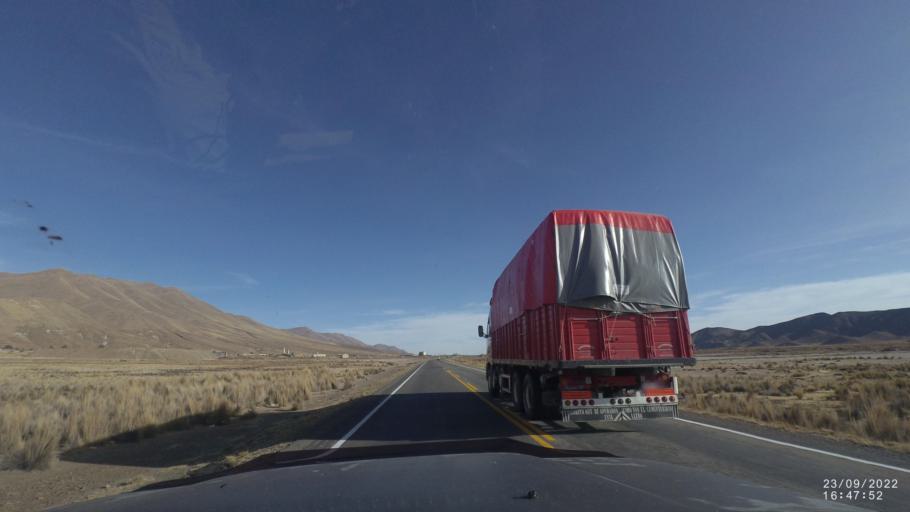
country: BO
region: Oruro
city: Poopo
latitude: -18.3738
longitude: -66.9802
